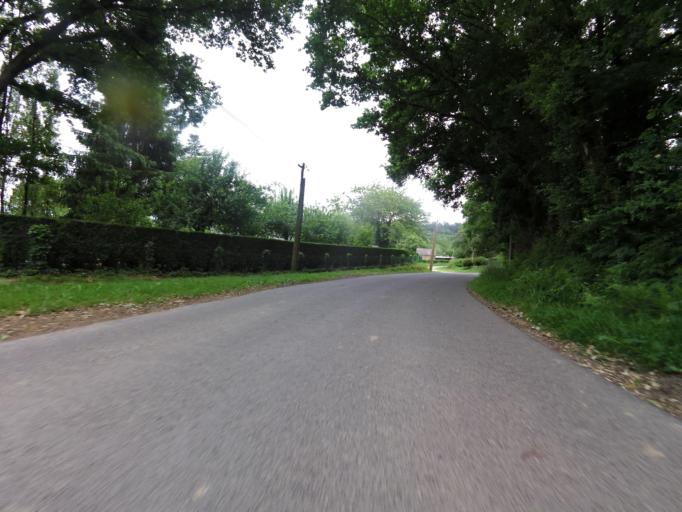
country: FR
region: Brittany
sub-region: Departement du Morbihan
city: Pluherlin
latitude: 47.7139
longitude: -2.3816
